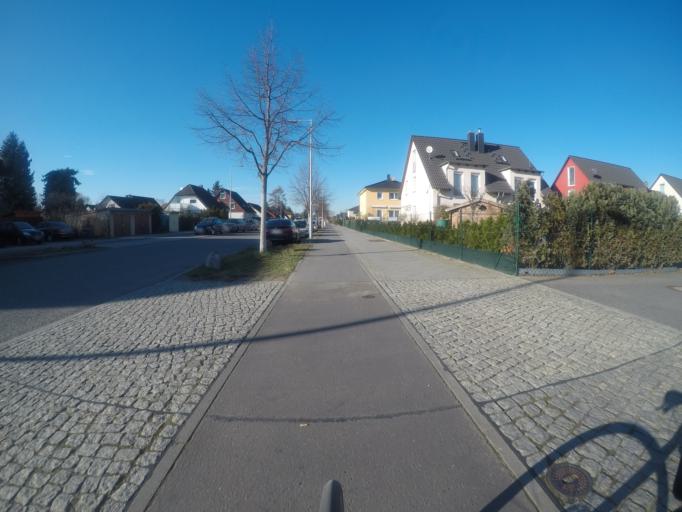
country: DE
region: Berlin
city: Johannisthal
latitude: 52.4311
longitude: 13.5124
